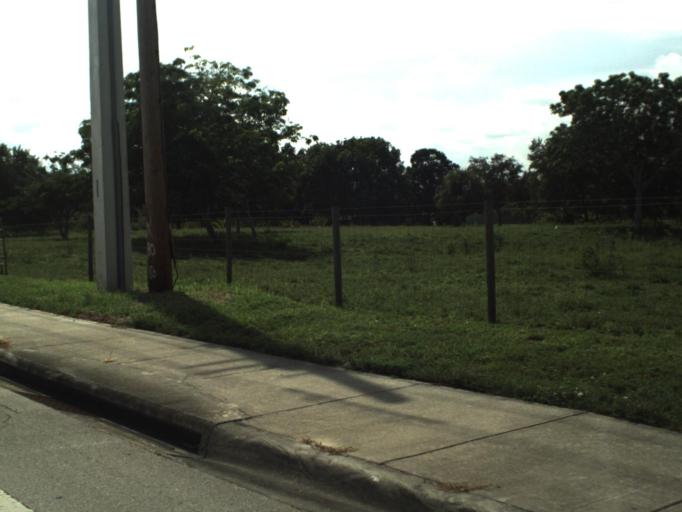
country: US
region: Florida
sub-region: Broward County
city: Cooper City
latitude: 26.0637
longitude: -80.2957
